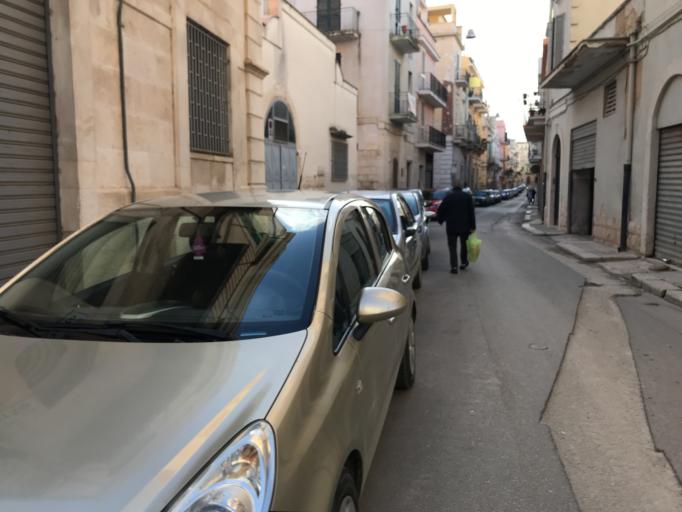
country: IT
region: Apulia
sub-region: Provincia di Bari
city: Corato
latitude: 41.1498
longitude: 16.4119
